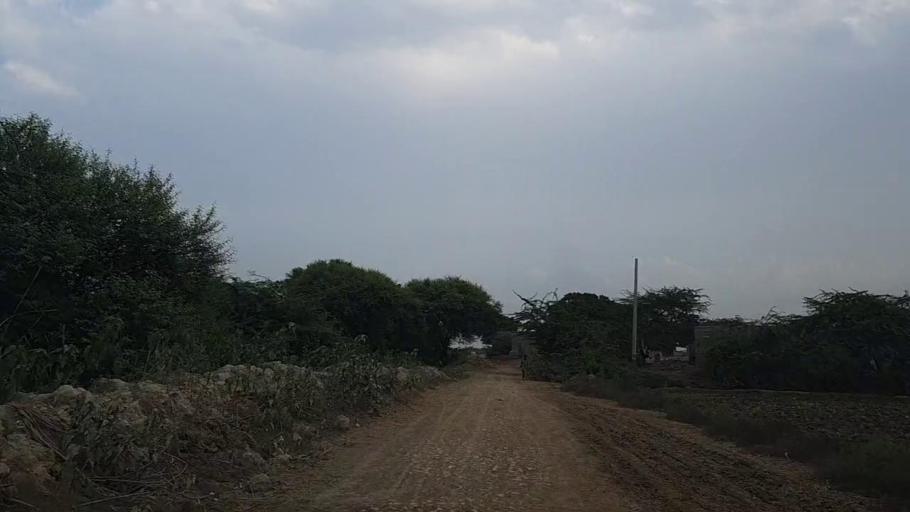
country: PK
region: Sindh
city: Daro Mehar
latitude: 24.7633
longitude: 68.1544
